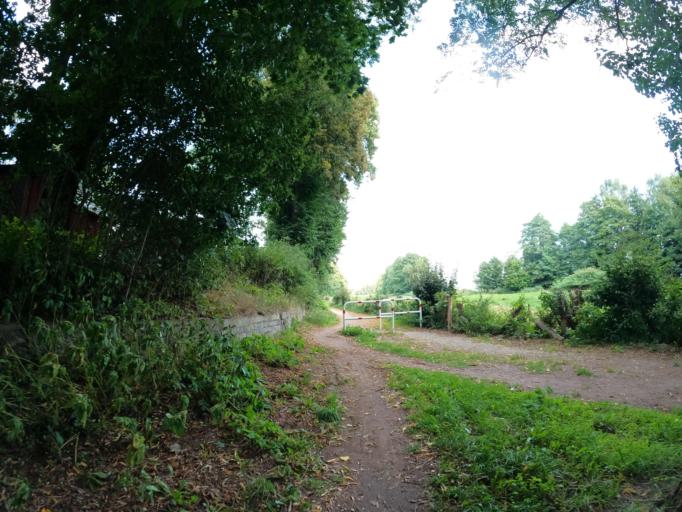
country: DE
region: Mecklenburg-Vorpommern
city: Malchow
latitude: 53.4892
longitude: 12.4352
